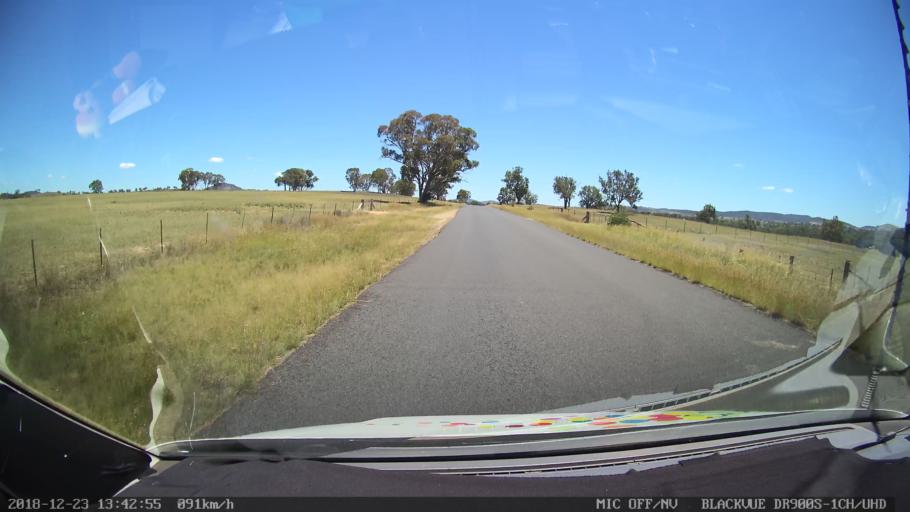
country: AU
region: New South Wales
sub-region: Tamworth Municipality
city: Manilla
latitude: -30.4818
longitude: 151.1572
